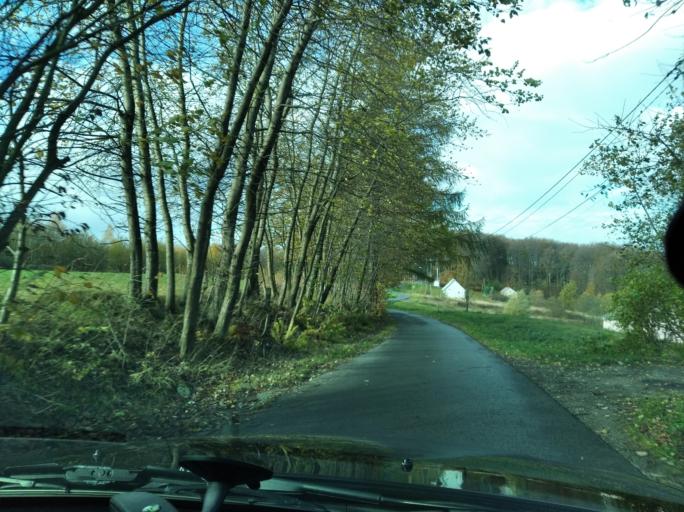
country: PL
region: Subcarpathian Voivodeship
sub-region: Powiat debicki
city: Debica
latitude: 50.0297
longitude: 21.4599
